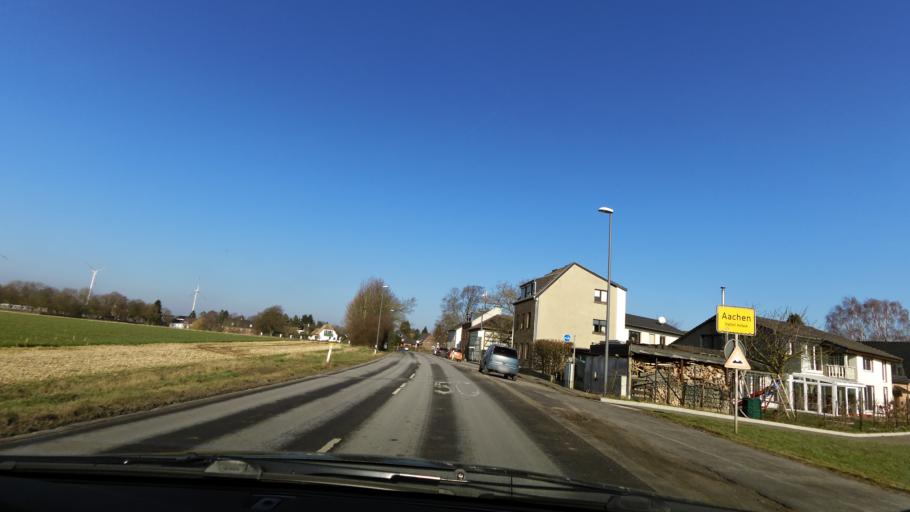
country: NL
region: Limburg
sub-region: Gemeente Kerkrade
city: Kerkrade
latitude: 50.8304
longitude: 6.0492
